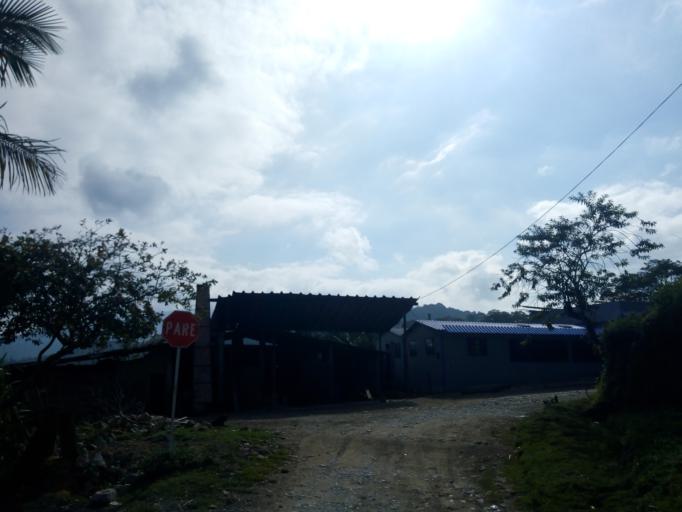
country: CO
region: Boyaca
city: Moniquira
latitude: 5.8859
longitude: -73.5129
